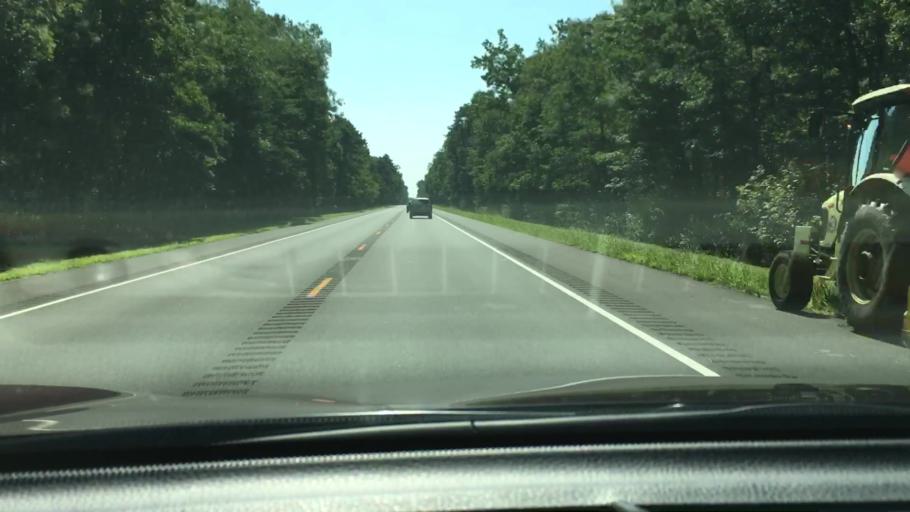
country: US
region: New Jersey
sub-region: Cape May County
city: Woodbine
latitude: 39.3379
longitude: -74.8880
